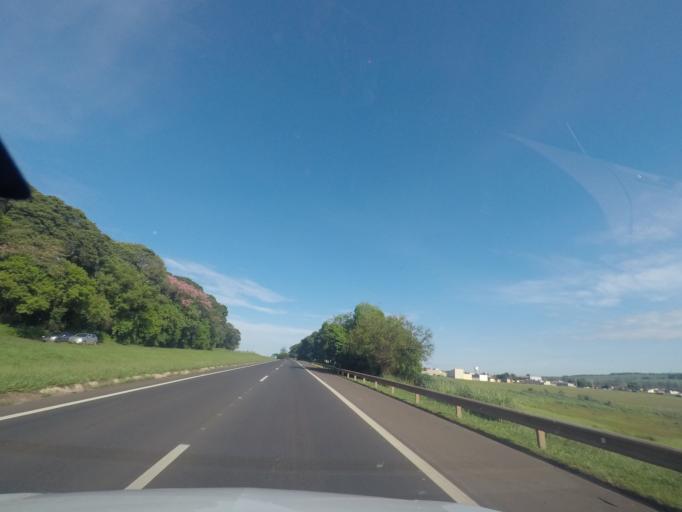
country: BR
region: Sao Paulo
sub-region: Santa Gertrudes
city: Santa Gertrudes
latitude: -22.4638
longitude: -47.5206
